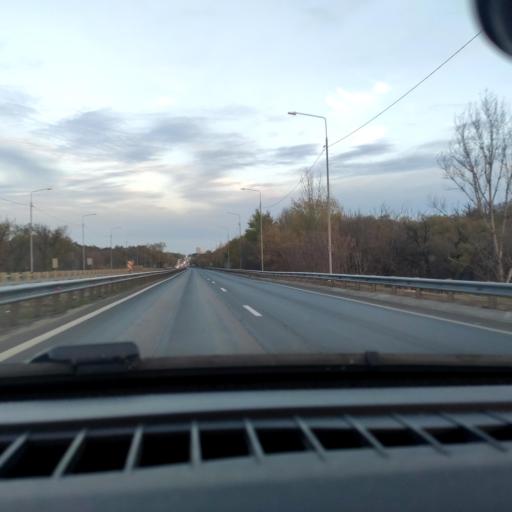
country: RU
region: Voronezj
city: Pridonskoy
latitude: 51.6502
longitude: 39.0793
